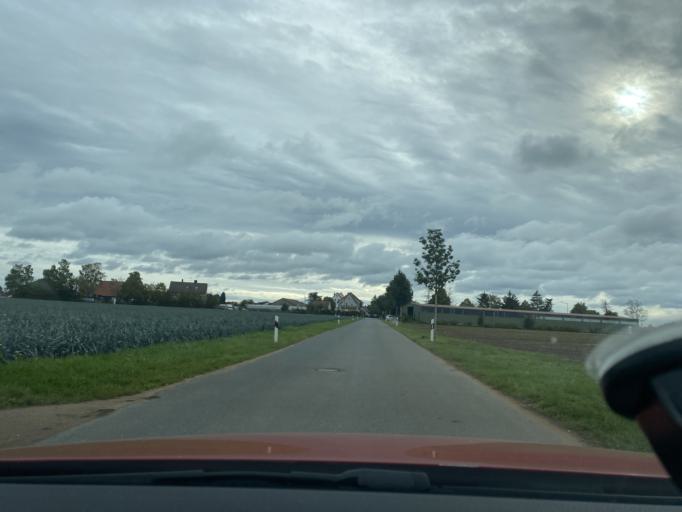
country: DE
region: Bavaria
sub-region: Regierungsbezirk Mittelfranken
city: Furth
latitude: 49.5007
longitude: 11.0050
